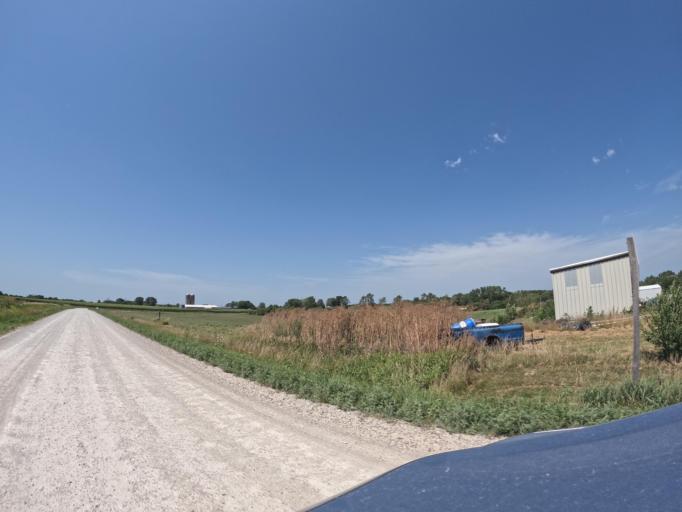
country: US
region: Iowa
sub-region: Henry County
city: Mount Pleasant
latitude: 40.9422
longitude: -91.6530
